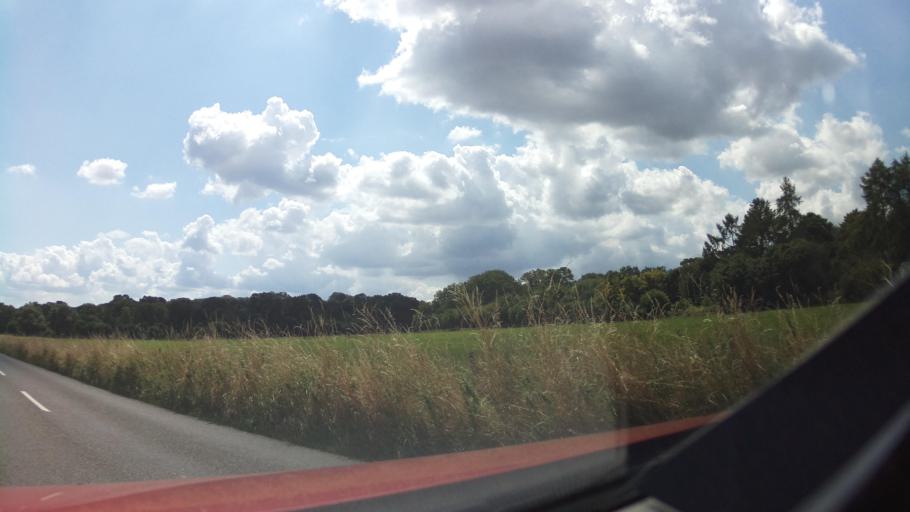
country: GB
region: England
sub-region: Borough of Swindon
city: Bishopstone
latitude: 51.5464
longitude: -1.5949
